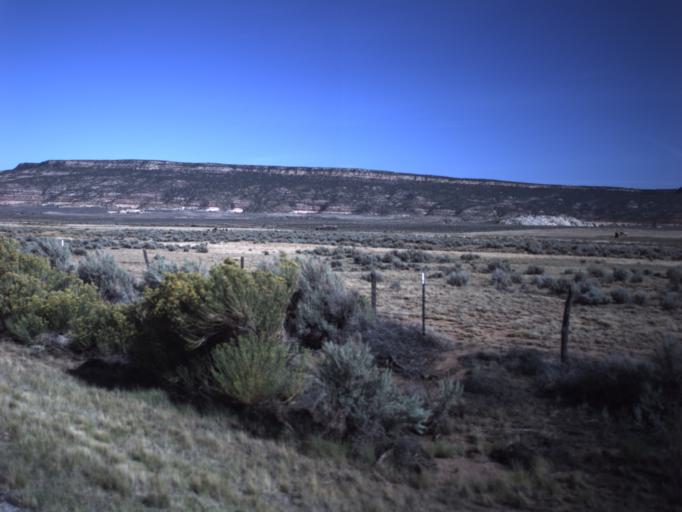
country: US
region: Utah
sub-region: San Juan County
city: Monticello
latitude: 38.0643
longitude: -109.3870
